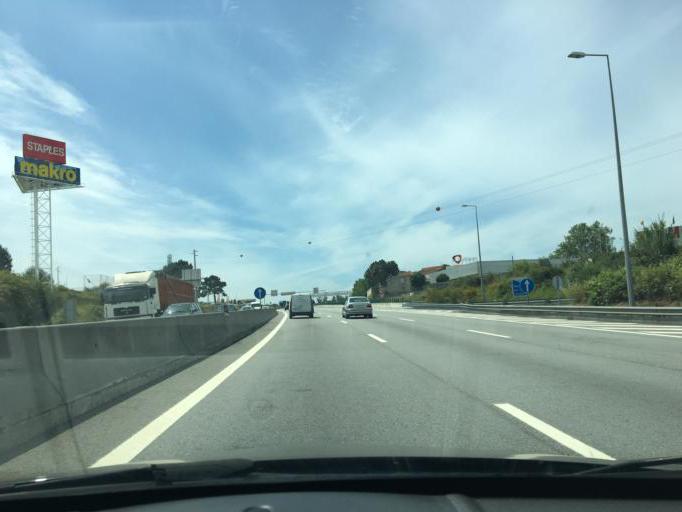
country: PT
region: Porto
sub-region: Maia
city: Leca do Bailio
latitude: 41.2018
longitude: -8.6275
